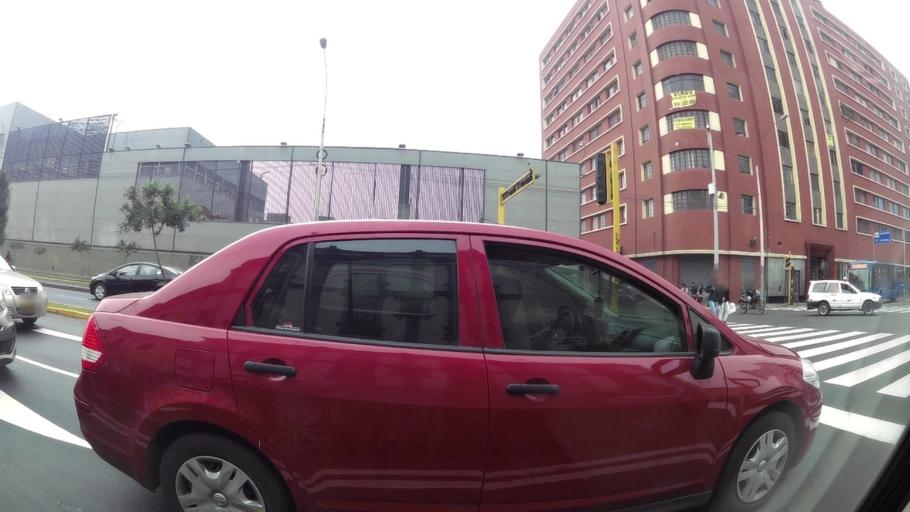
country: PE
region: Lima
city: Lima
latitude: -12.0475
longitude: -77.0383
